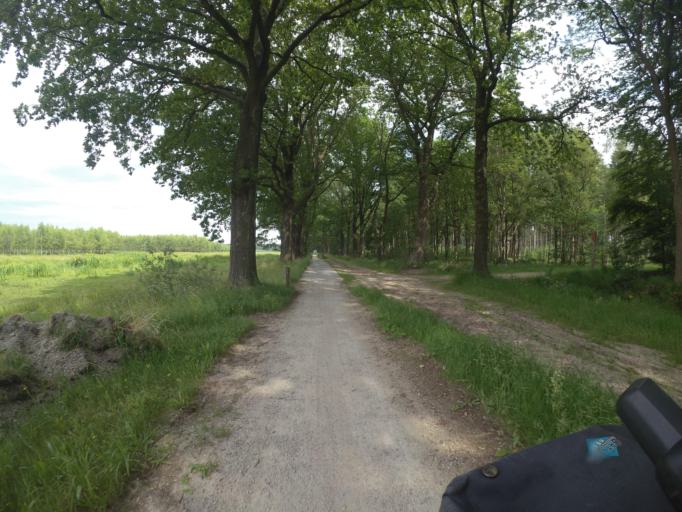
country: NL
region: Drenthe
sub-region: Gemeente Assen
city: Assen
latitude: 53.0075
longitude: 6.4417
